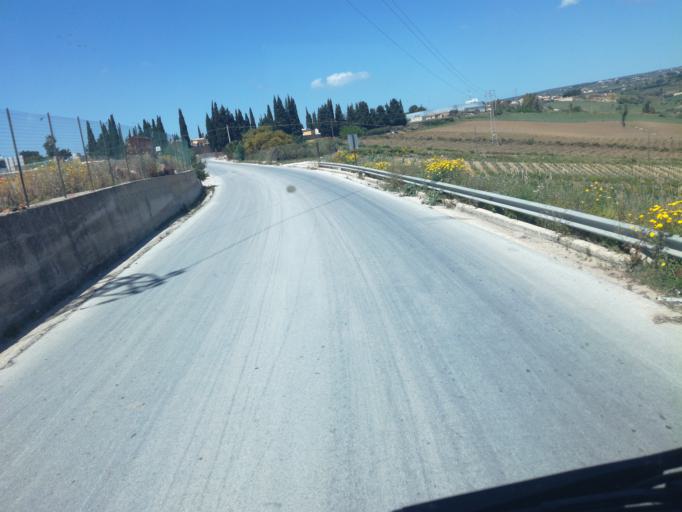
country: IT
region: Sicily
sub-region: Agrigento
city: Menfi
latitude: 37.5968
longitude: 12.9785
